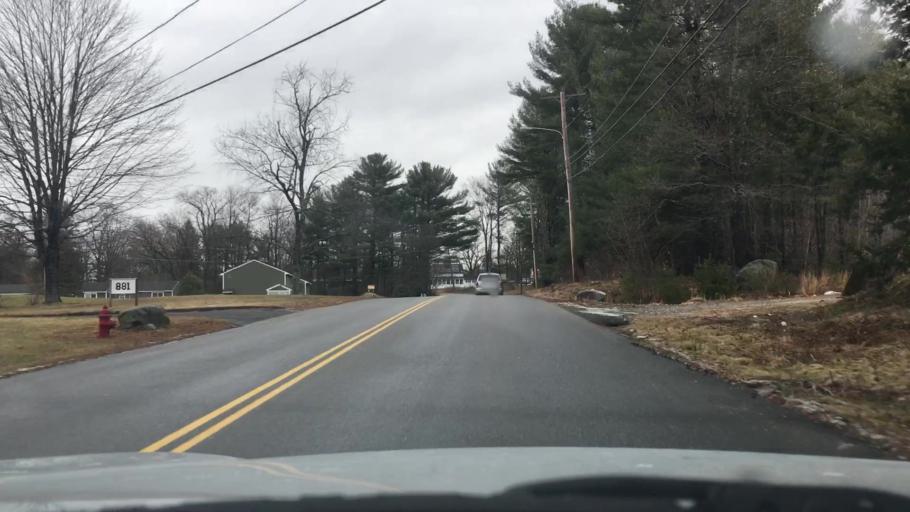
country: US
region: Massachusetts
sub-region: Franklin County
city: Orange
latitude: 42.5703
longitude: -72.2676
